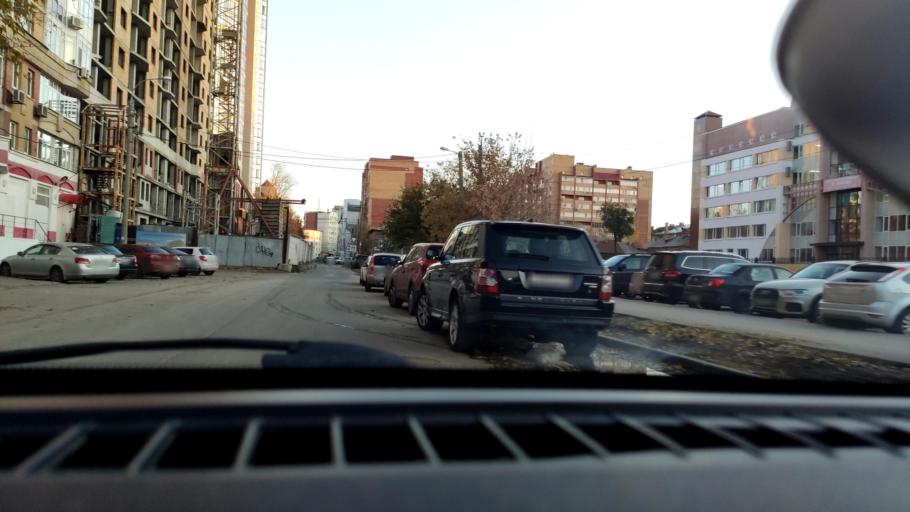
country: RU
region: Samara
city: Samara
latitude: 53.1949
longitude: 50.1093
